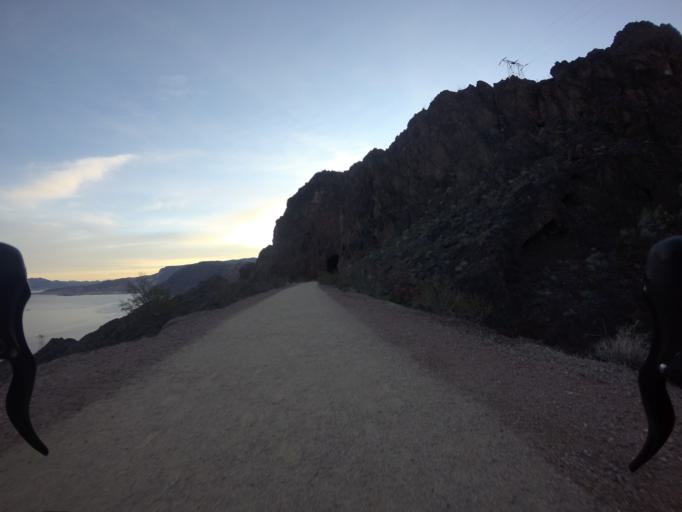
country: US
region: Nevada
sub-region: Clark County
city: Boulder City
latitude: 36.0161
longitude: -114.7672
